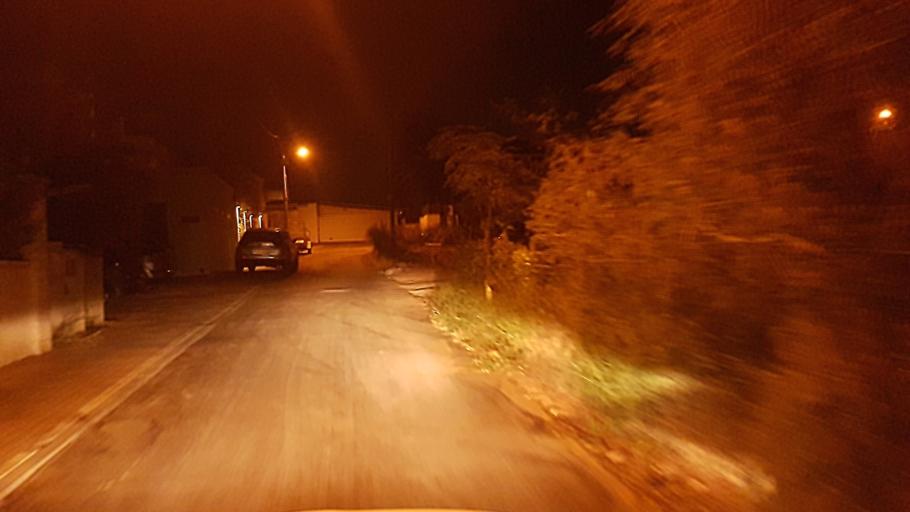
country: IL
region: Central District
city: Hod HaSharon
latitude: 32.1632
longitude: 34.8766
